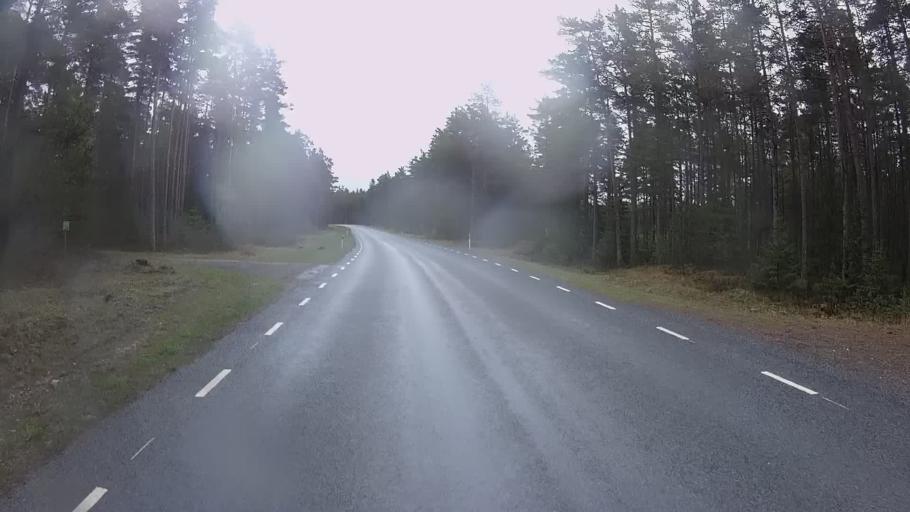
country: EE
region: Hiiumaa
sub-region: Kaerdla linn
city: Kardla
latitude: 58.9109
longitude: 22.3894
